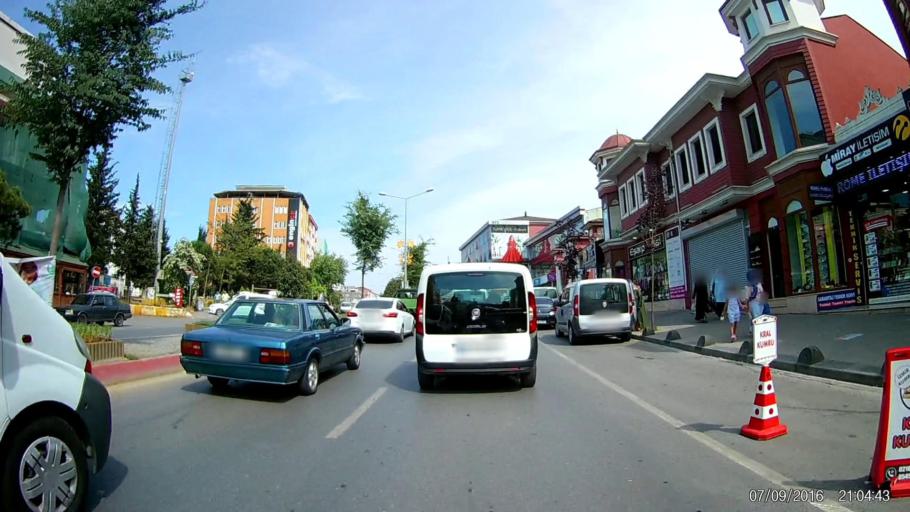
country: TR
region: Istanbul
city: Sultanbeyli
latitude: 40.9690
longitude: 29.2584
